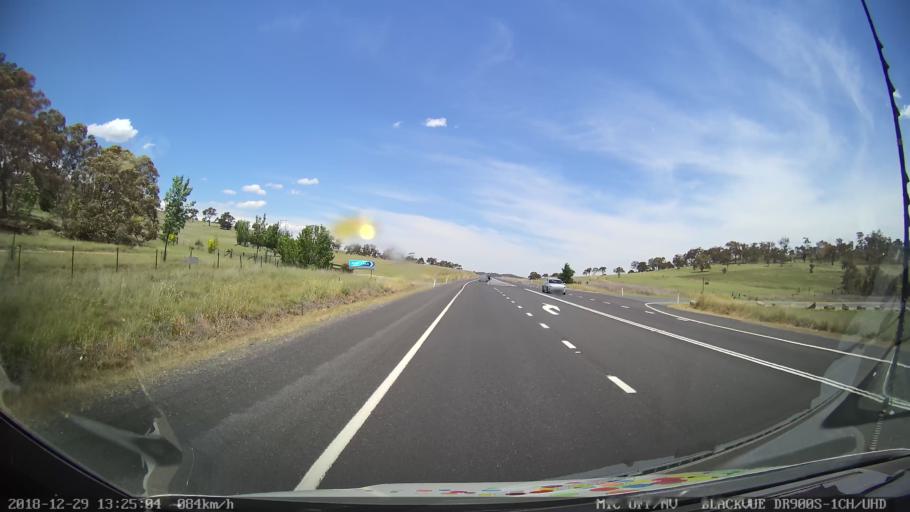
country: AU
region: New South Wales
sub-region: Cooma-Monaro
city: Cooma
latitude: -35.8376
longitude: 149.1622
